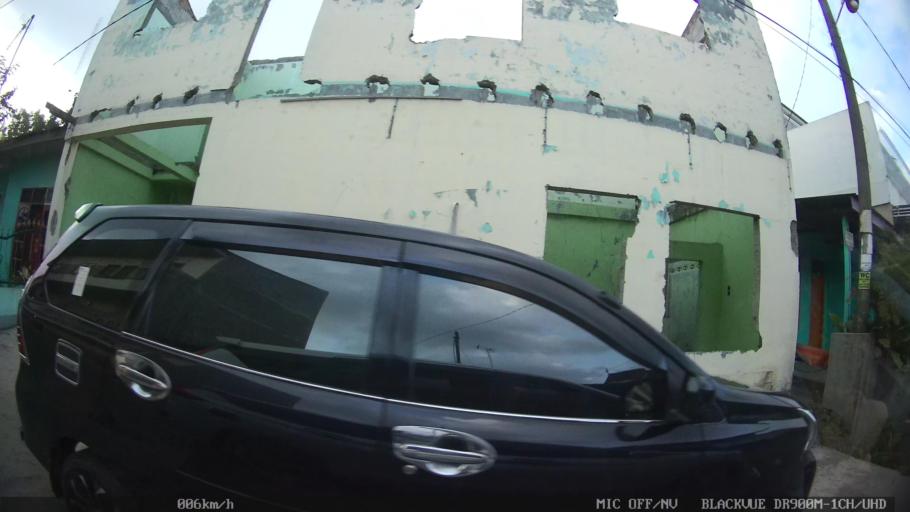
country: ID
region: North Sumatra
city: Medan
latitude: 3.5911
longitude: 98.7415
